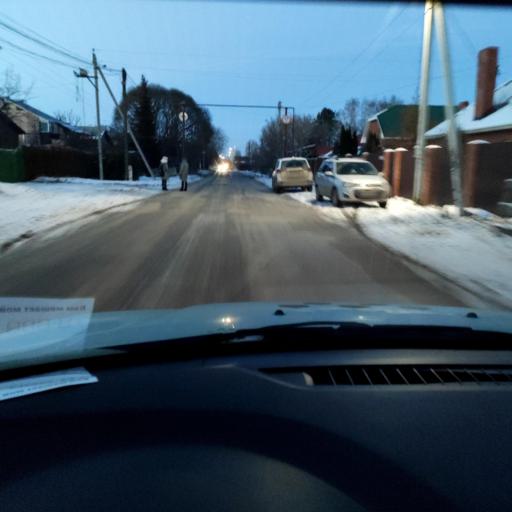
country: RU
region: Samara
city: Tol'yatti
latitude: 53.5635
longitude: 49.3895
